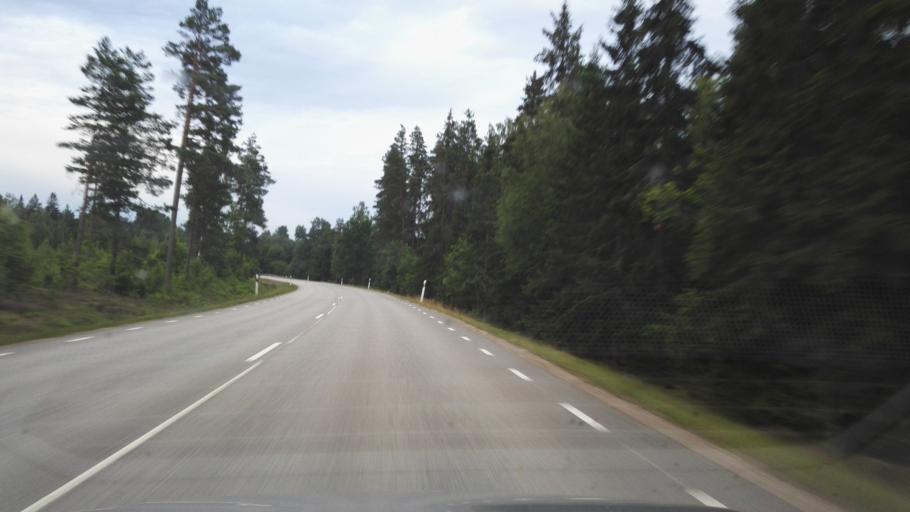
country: SE
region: Kronoberg
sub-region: Vaxjo Kommun
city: Braas
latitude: 57.0413
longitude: 15.0650
